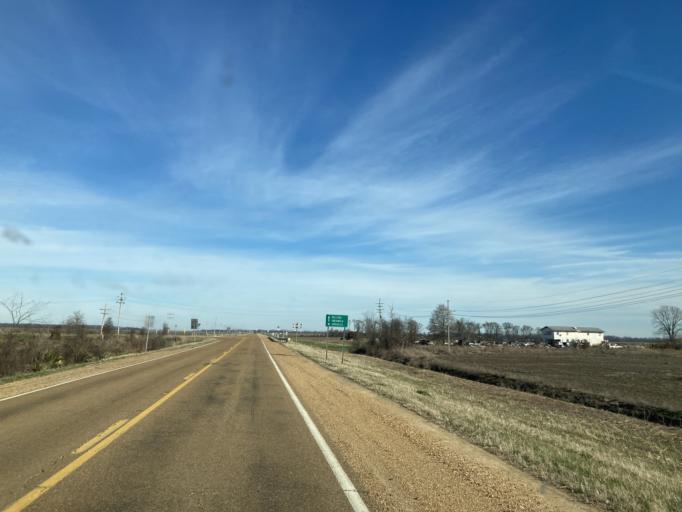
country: US
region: Mississippi
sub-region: Humphreys County
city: Belzoni
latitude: 32.9943
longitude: -90.5884
